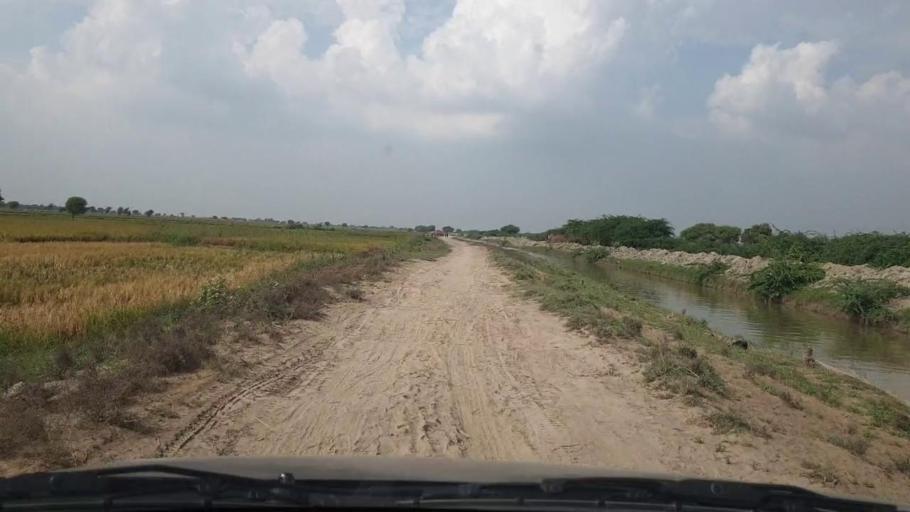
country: PK
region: Sindh
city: Badin
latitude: 24.5682
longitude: 68.6343
